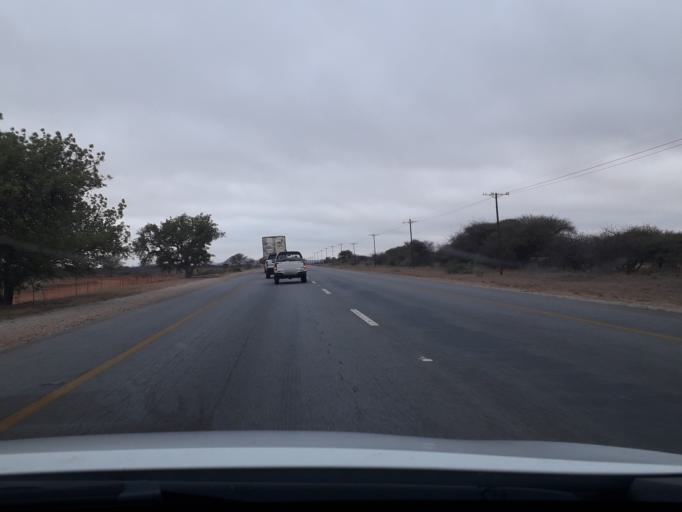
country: ZA
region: Limpopo
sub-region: Capricorn District Municipality
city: Mankoeng
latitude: -23.5786
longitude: 29.6706
